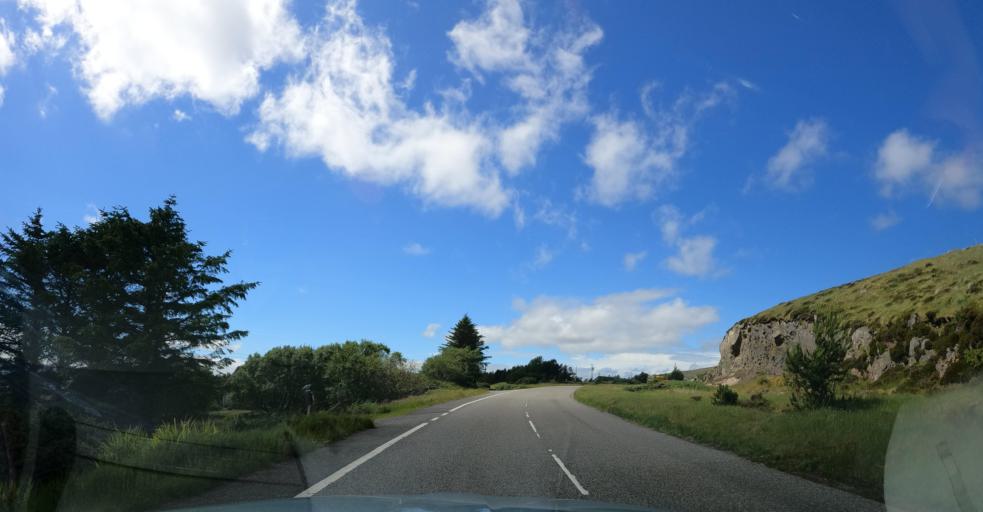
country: GB
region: Scotland
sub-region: Eilean Siar
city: Stornoway
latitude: 58.1659
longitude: -6.5596
